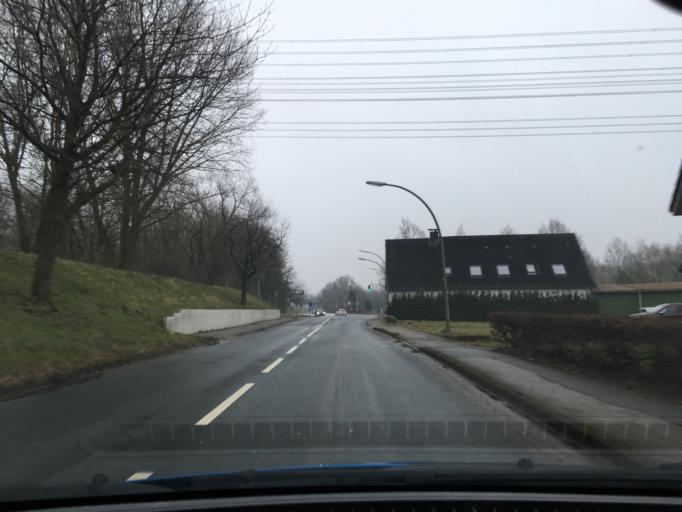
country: DE
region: Hamburg
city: Altona
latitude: 53.4959
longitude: 9.9080
